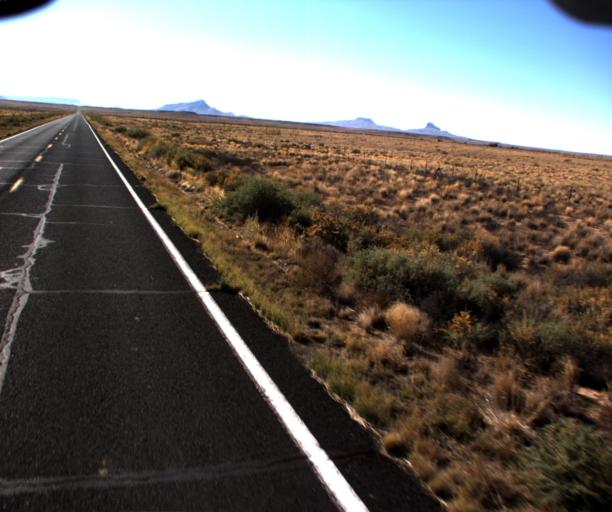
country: US
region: Arizona
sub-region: Navajo County
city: Dilkon
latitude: 35.5815
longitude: -110.4641
